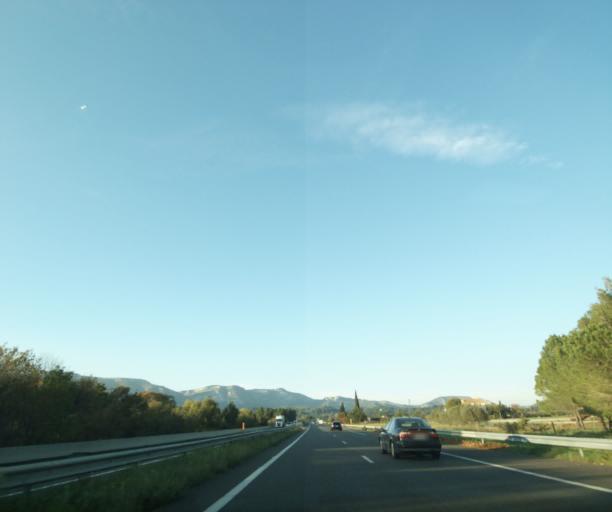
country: FR
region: Provence-Alpes-Cote d'Azur
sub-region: Departement des Bouches-du-Rhone
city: Aubagne
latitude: 43.3128
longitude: 5.5914
